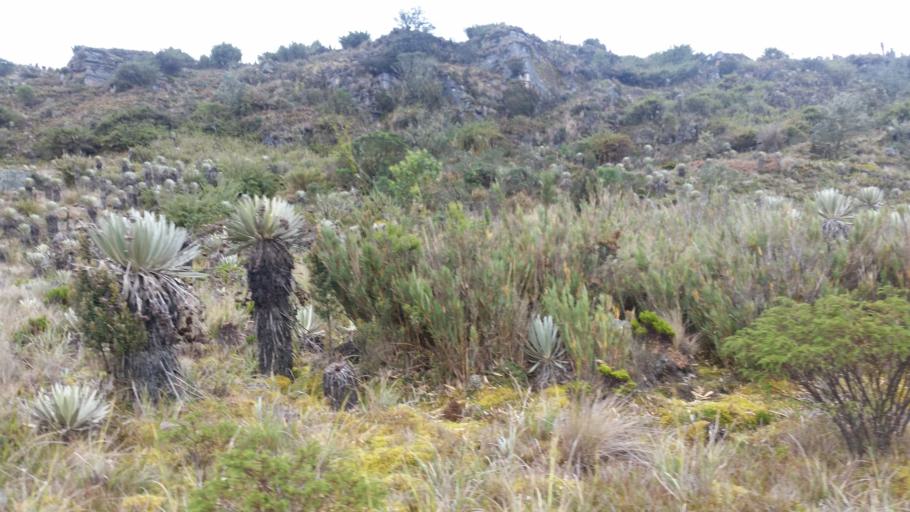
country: CO
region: Cundinamarca
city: Pasca
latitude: 4.3672
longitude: -74.2189
